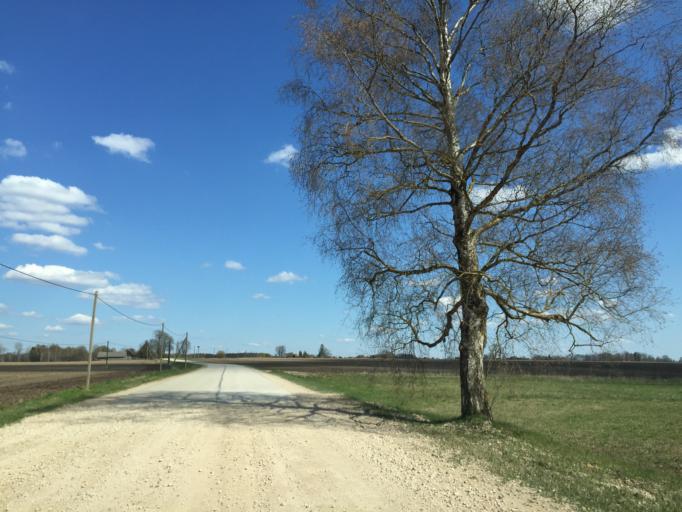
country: LV
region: Seja
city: Loja
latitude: 57.2639
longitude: 24.5666
